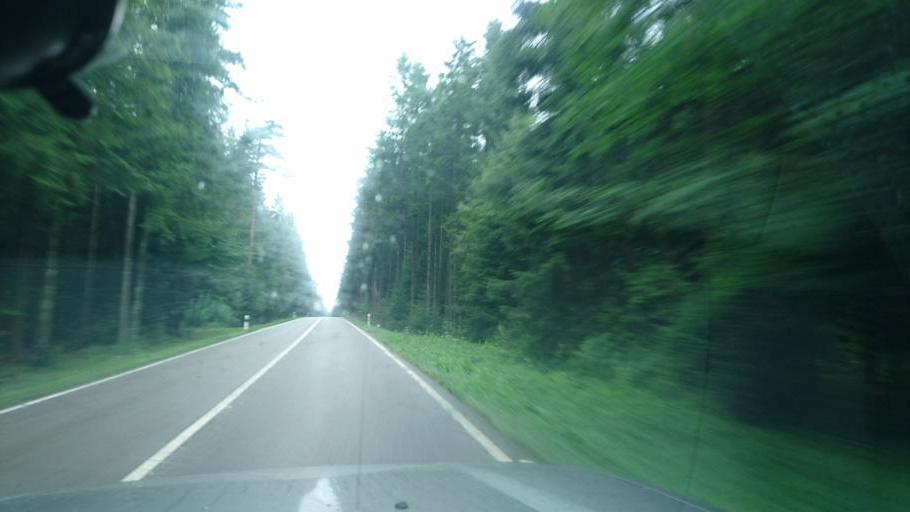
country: DE
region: Baden-Wuerttemberg
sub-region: Karlsruhe Region
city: Baiersbronn
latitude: 48.5447
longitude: 8.4286
